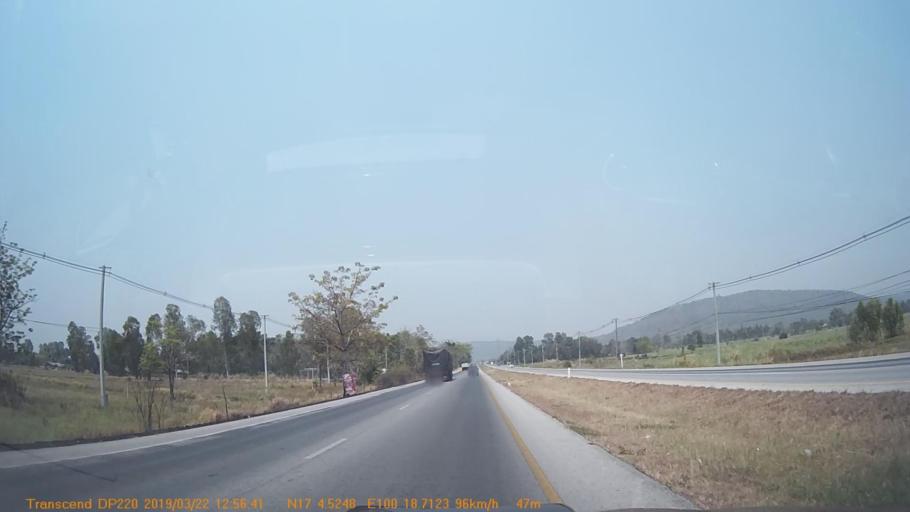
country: TH
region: Phitsanulok
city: Wat Bot
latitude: 17.0757
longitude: 100.3119
